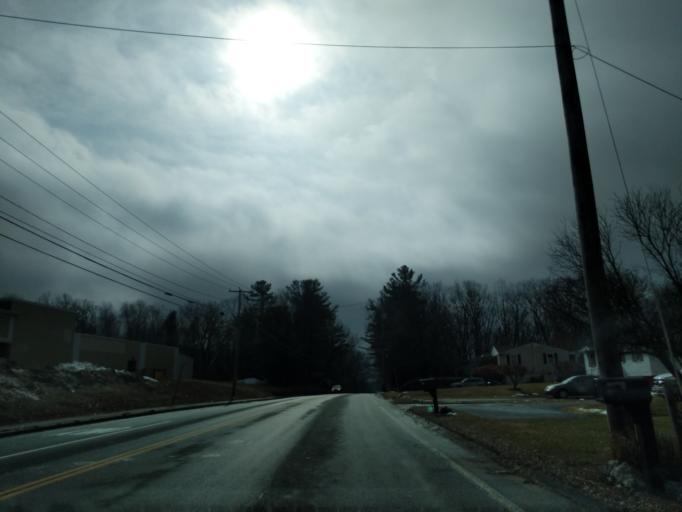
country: US
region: Massachusetts
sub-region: Worcester County
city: Webster
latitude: 42.0707
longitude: -71.8665
